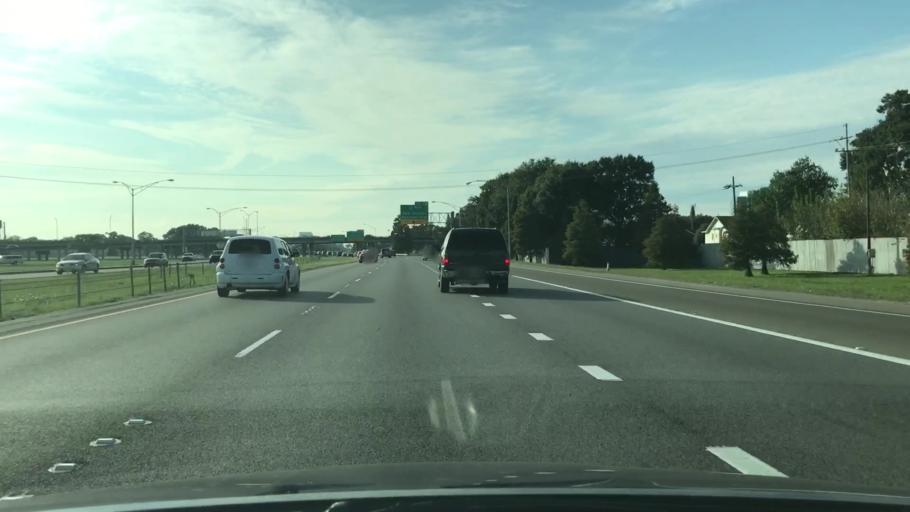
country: US
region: Louisiana
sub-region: Jefferson Parish
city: Metairie
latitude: 29.9940
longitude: -90.1147
